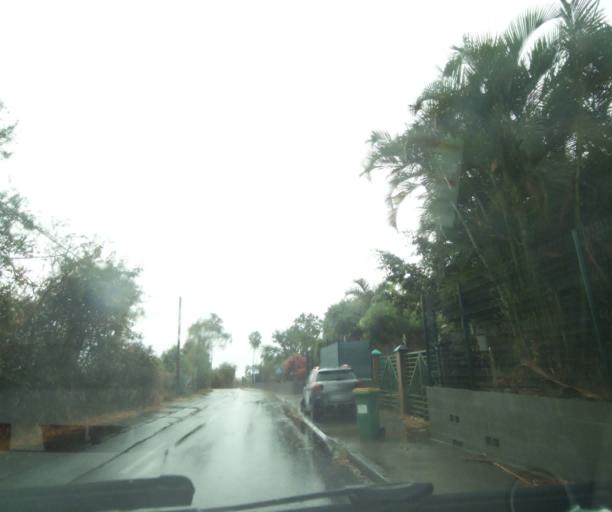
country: RE
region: Reunion
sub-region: Reunion
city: Le Port
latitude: -20.9721
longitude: 55.3154
